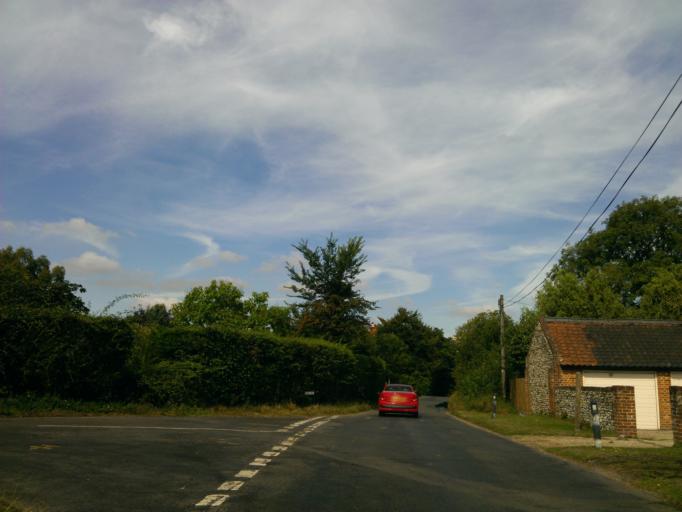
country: GB
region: England
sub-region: Essex
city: Sible Hedingham
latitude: 51.9761
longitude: 0.6167
